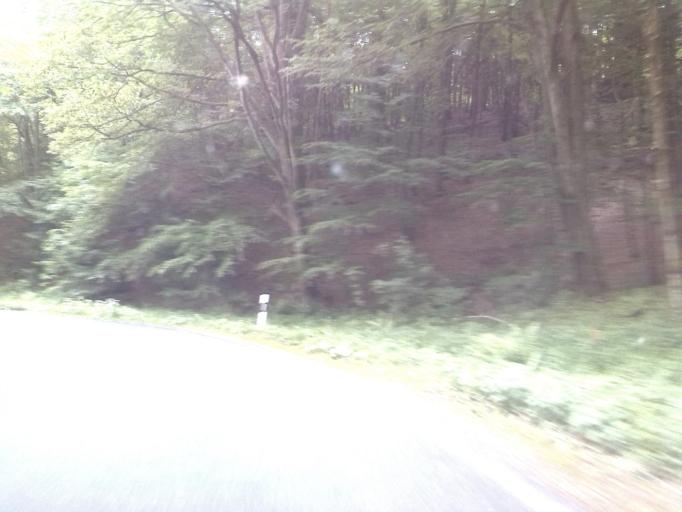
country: DE
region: Hesse
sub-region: Regierungsbezirk Darmstadt
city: Lindenfels
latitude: 49.6918
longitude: 8.7918
